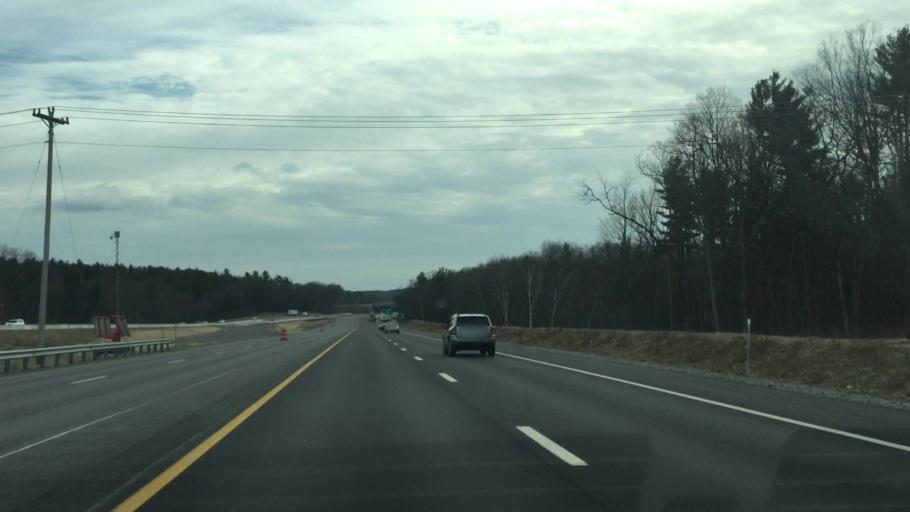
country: US
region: New Hampshire
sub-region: Rockingham County
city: Derry
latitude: 42.8867
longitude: -71.3508
